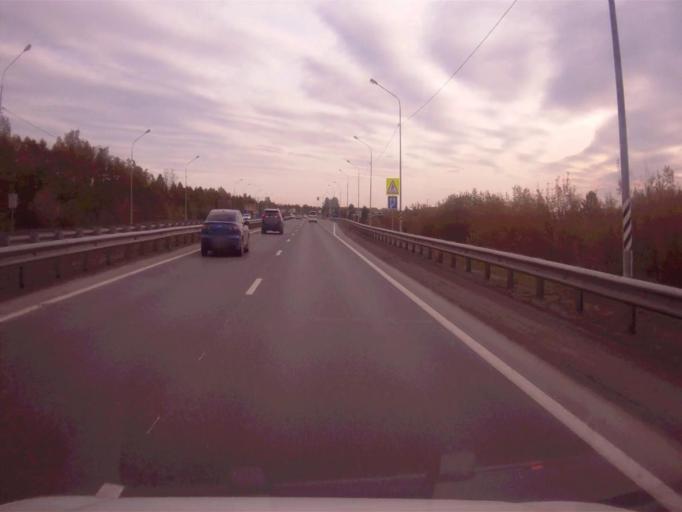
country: RU
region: Chelyabinsk
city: Novosineglazovskiy
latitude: 55.0331
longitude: 61.4440
